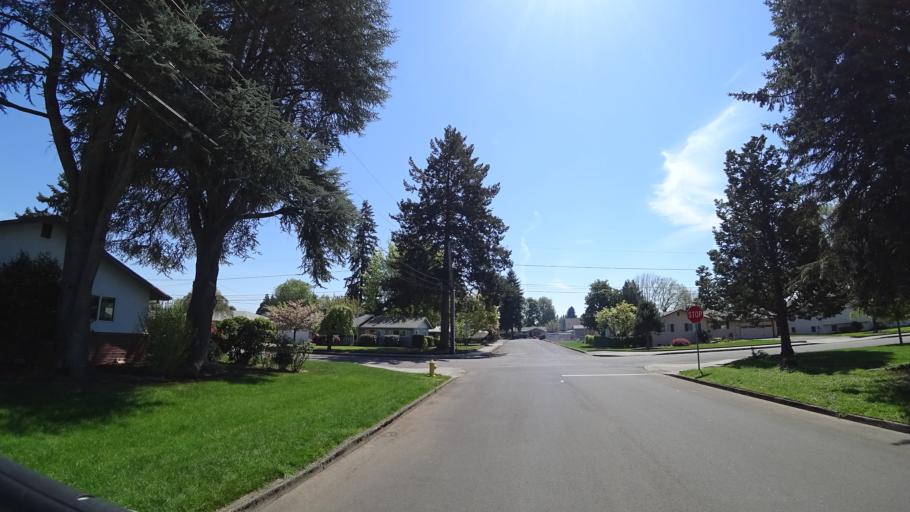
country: US
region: Oregon
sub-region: Washington County
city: Hillsboro
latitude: 45.5117
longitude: -122.9640
